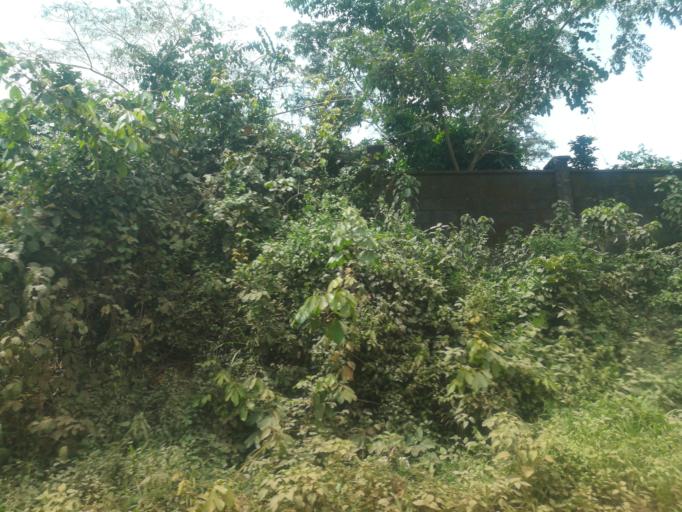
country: NG
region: Oyo
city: Moniya
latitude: 7.4658
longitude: 3.9546
